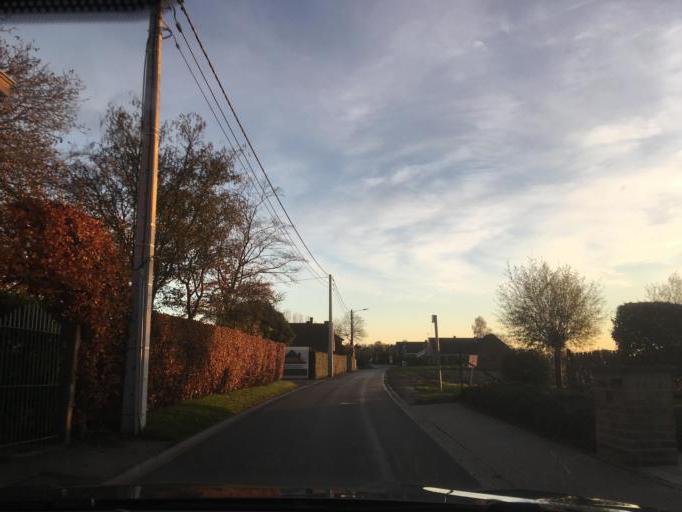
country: BE
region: Flanders
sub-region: Provincie West-Vlaanderen
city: Ardooie
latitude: 50.9778
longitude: 3.1904
